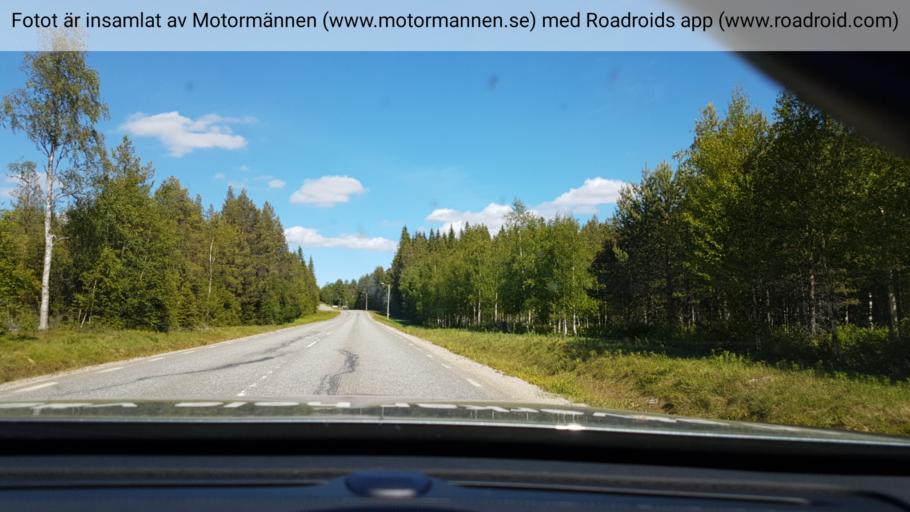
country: SE
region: Vaesterbotten
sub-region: Lycksele Kommun
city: Lycksele
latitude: 64.6187
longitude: 18.3400
